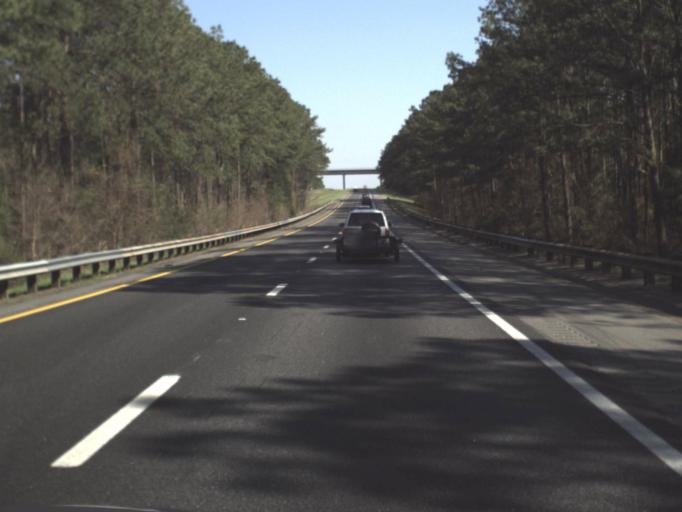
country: US
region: Florida
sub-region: Gadsden County
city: Chattahoochee
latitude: 30.6263
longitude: -84.8527
